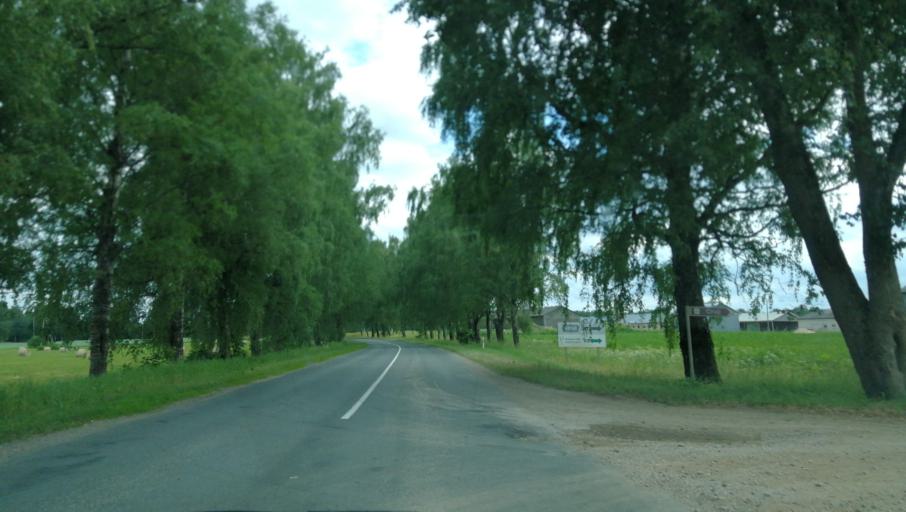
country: LV
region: Rujienas
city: Rujiena
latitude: 57.8678
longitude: 25.3690
